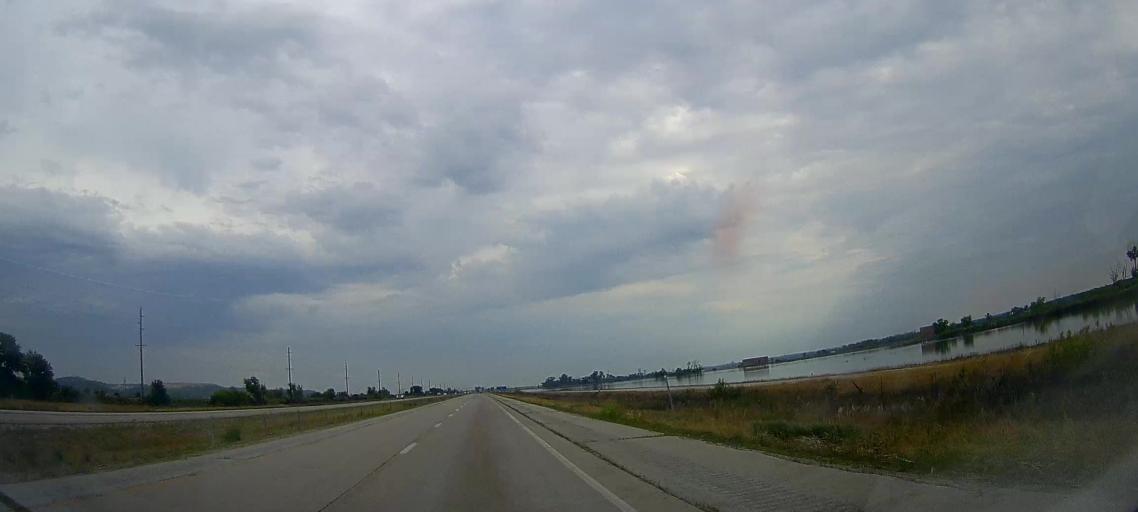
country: US
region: Iowa
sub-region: Pottawattamie County
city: Carter Lake
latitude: 41.3827
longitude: -95.8997
